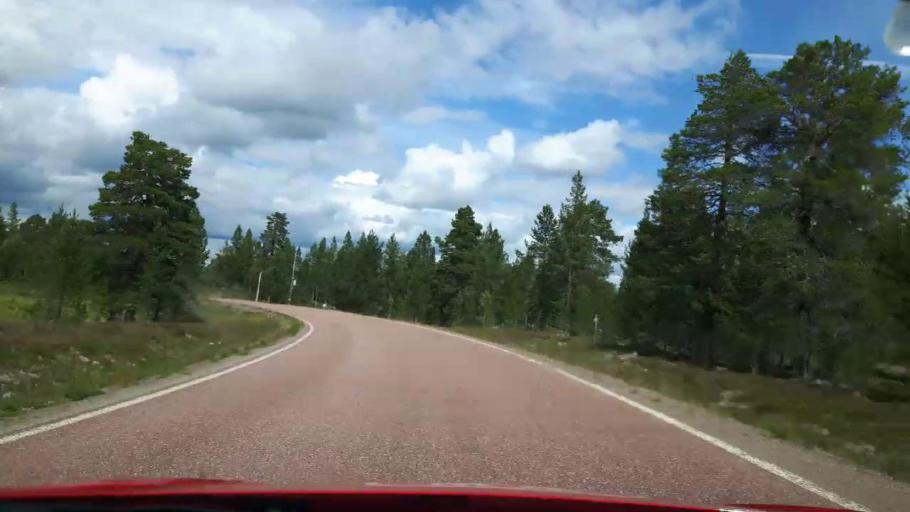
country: NO
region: Hedmark
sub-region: Trysil
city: Innbygda
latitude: 62.0920
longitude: 12.9743
